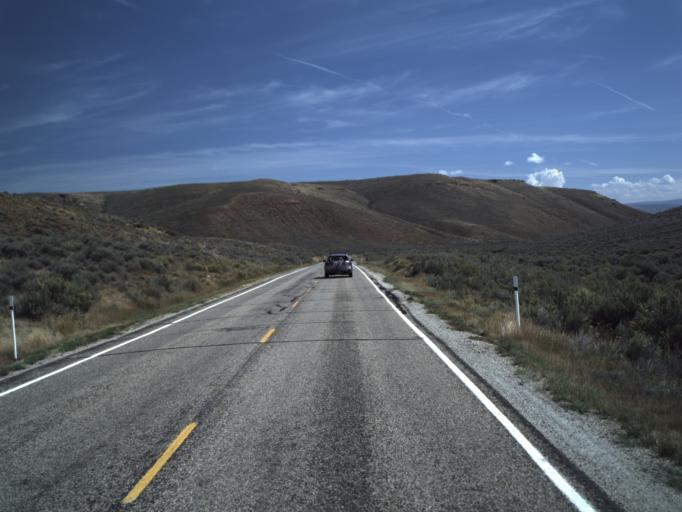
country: US
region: Utah
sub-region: Rich County
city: Randolph
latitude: 41.7766
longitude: -111.1871
